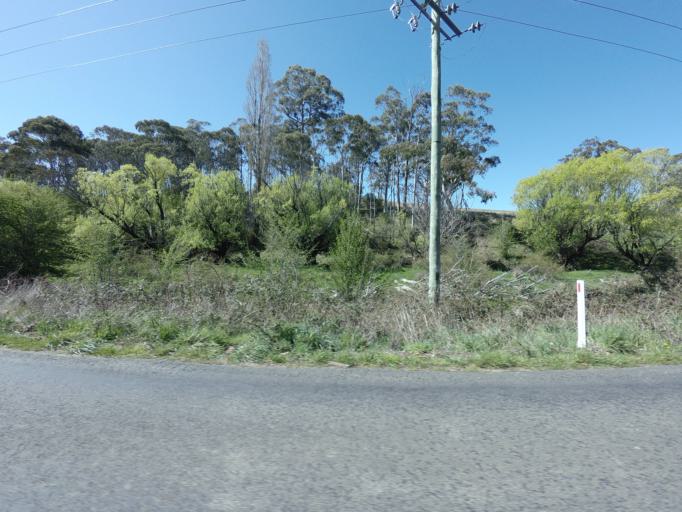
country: AU
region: Tasmania
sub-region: Derwent Valley
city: New Norfolk
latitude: -42.6265
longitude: 146.7238
